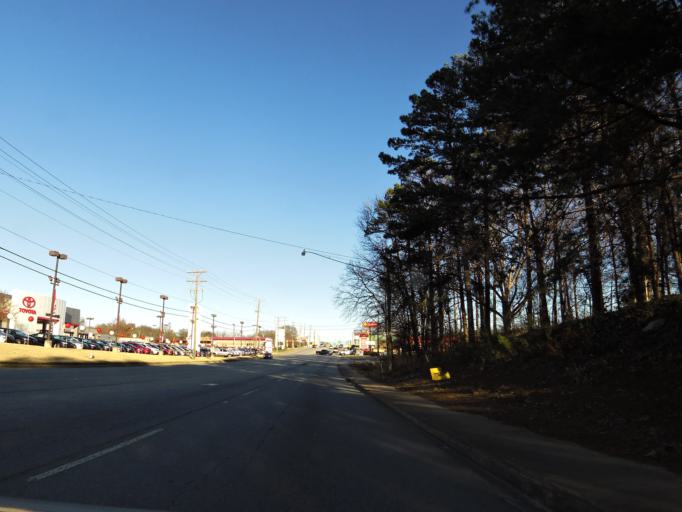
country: US
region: South Carolina
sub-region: Spartanburg County
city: Fairforest
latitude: 34.9193
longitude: -81.9973
